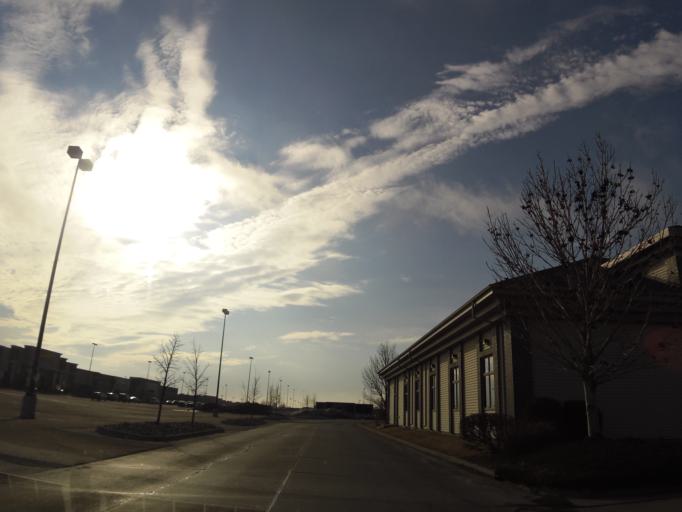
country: US
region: North Dakota
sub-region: Grand Forks County
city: Grand Forks
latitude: 47.8880
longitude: -97.0735
